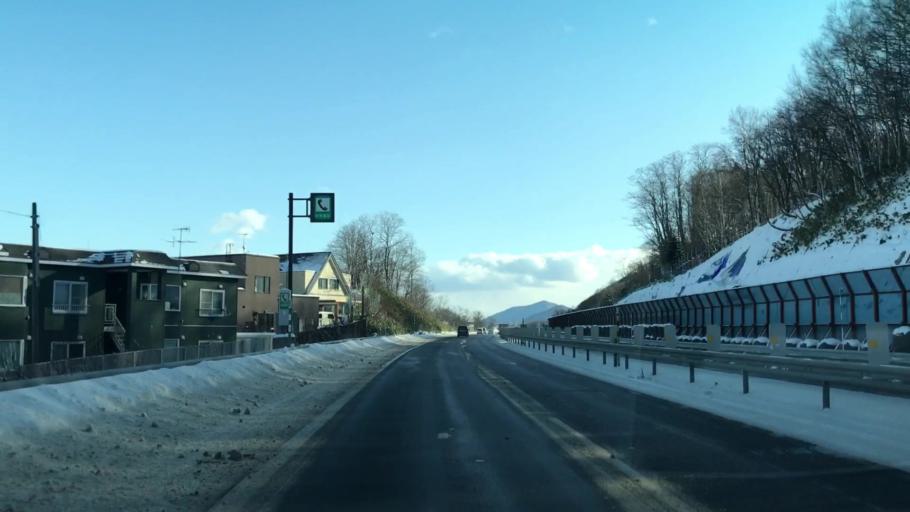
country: JP
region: Hokkaido
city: Sapporo
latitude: 43.1145
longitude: 141.2359
